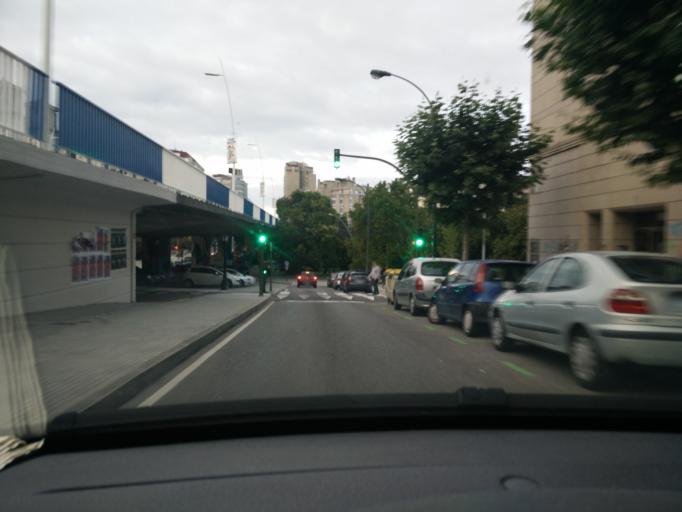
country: ES
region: Galicia
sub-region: Provincia da Coruna
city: A Coruna
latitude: 43.3564
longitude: -8.4058
